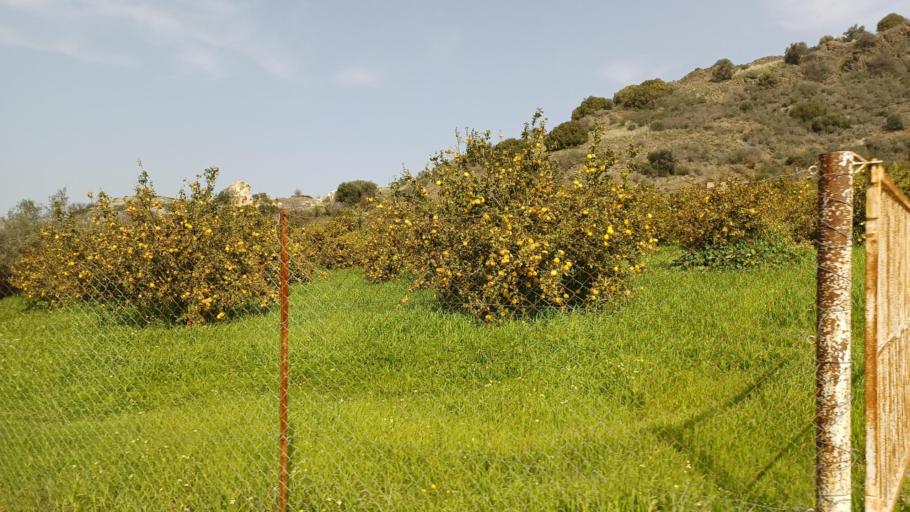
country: CY
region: Limassol
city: Pissouri
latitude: 34.7627
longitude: 32.6408
